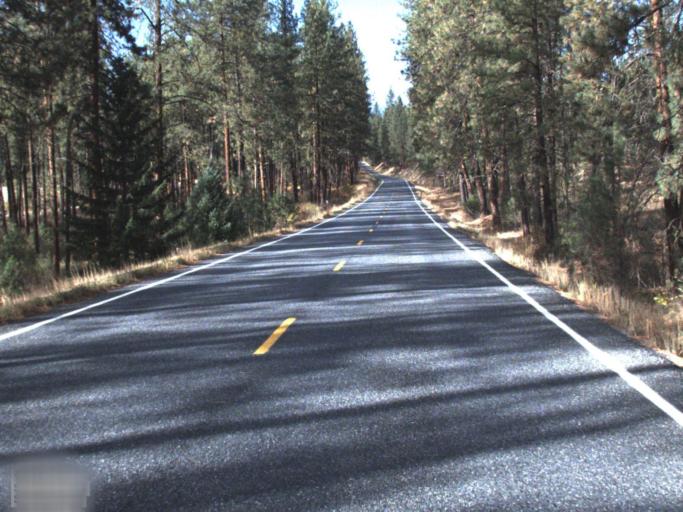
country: US
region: Washington
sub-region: Stevens County
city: Kettle Falls
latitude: 48.2939
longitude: -118.1433
